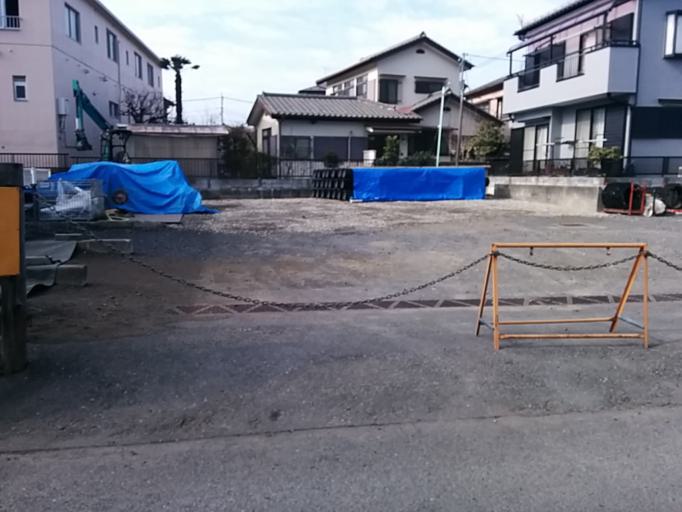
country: JP
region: Saitama
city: Kawagoe
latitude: 35.9219
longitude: 139.4909
